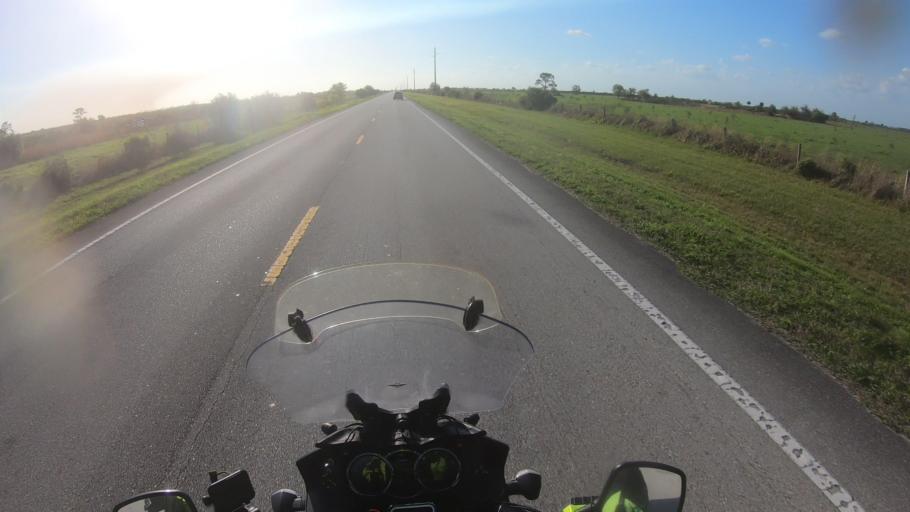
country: US
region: Florida
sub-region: Highlands County
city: Placid Lakes
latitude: 27.2088
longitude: -81.5094
